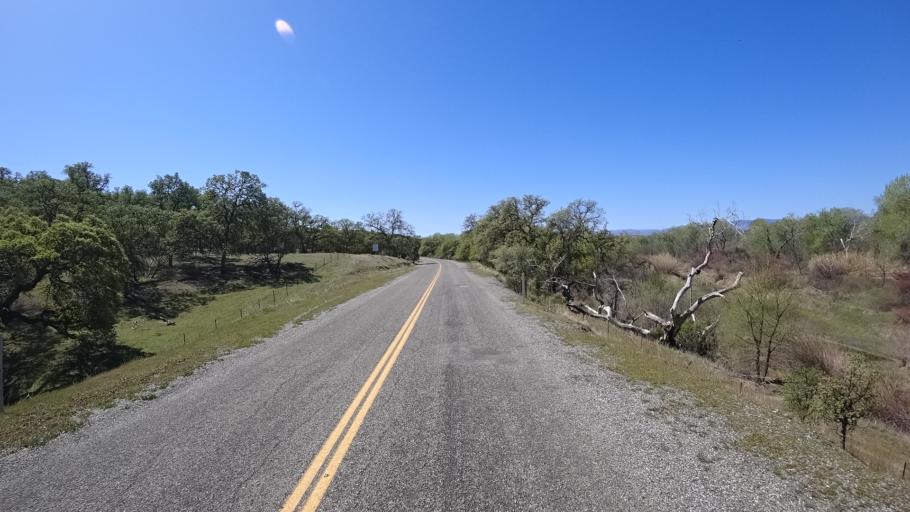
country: US
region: California
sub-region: Glenn County
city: Orland
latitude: 39.7396
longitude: -122.3895
